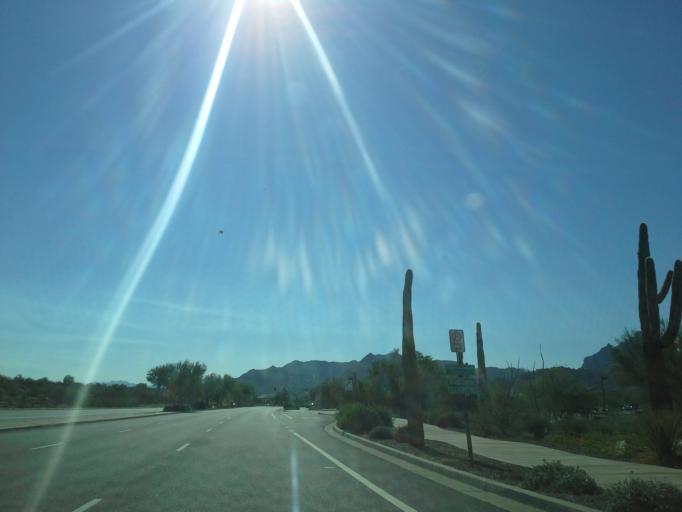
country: US
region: Arizona
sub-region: Maricopa County
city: Fountain Hills
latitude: 33.5762
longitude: -111.7197
